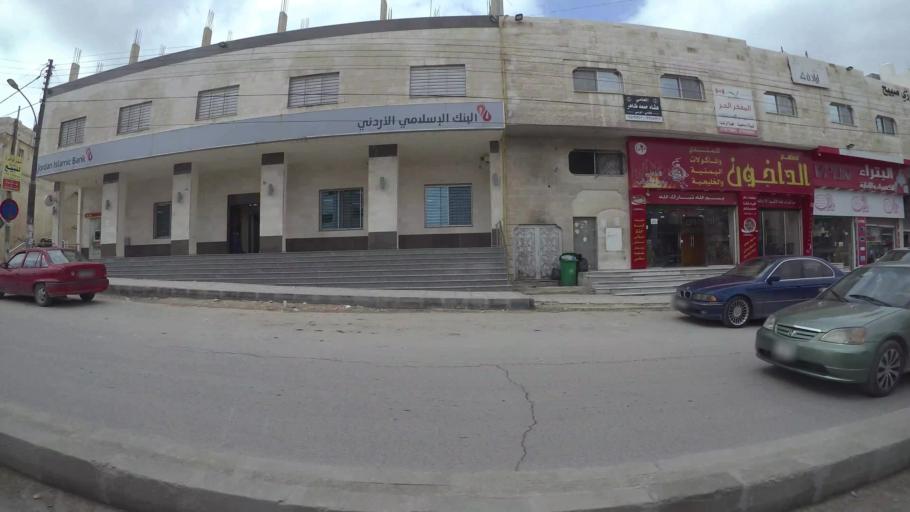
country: JO
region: Amman
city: Al Jubayhah
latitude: 32.0580
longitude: 35.8352
